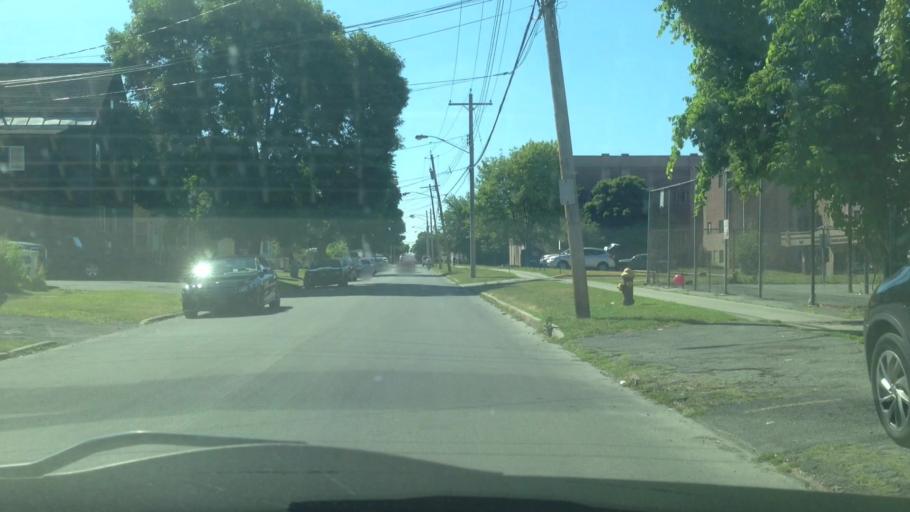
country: US
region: New York
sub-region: Oneida County
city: Utica
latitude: 43.0972
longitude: -75.2113
